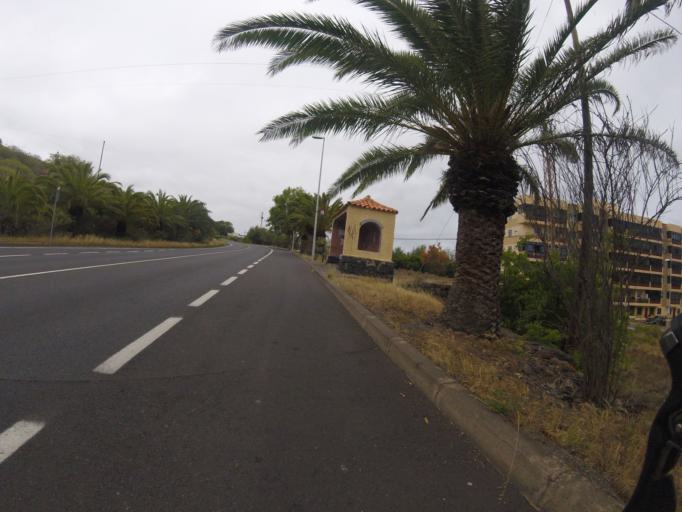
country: ES
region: Canary Islands
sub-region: Provincia de Santa Cruz de Tenerife
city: Tegueste
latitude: 28.5447
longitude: -16.3528
